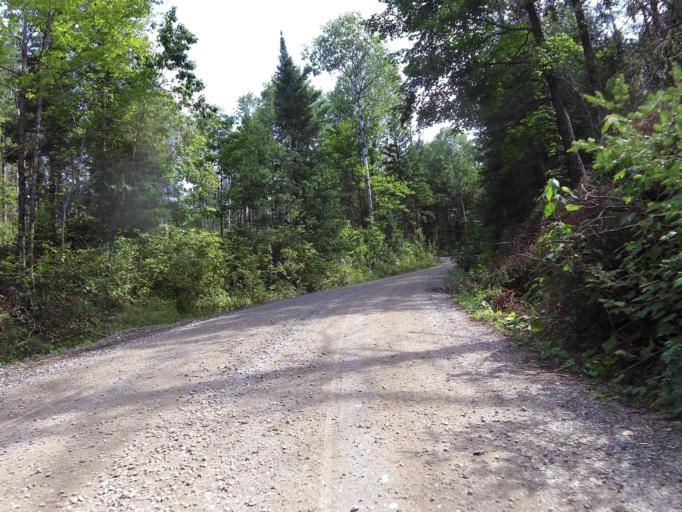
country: CA
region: Ontario
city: Renfrew
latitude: 45.1174
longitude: -76.7259
